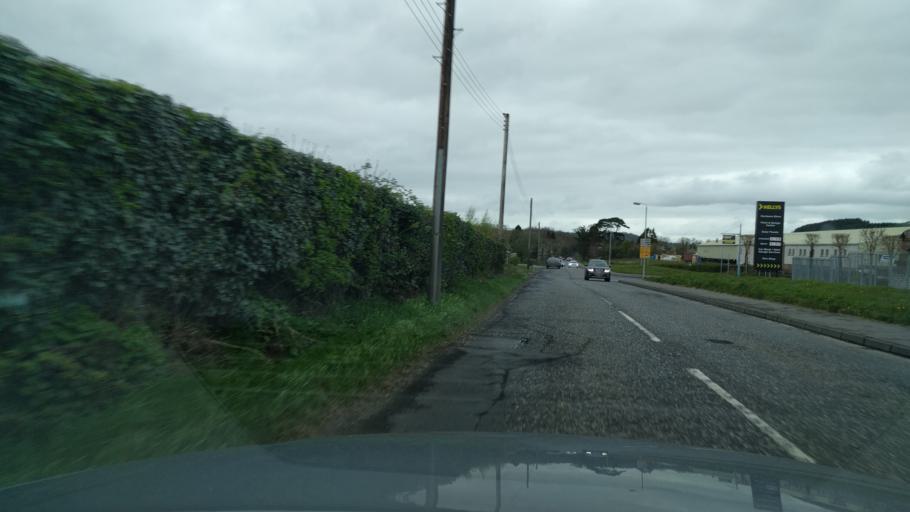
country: GB
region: Northern Ireland
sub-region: Down District
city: Warrenpoint
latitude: 54.1175
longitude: -6.2657
